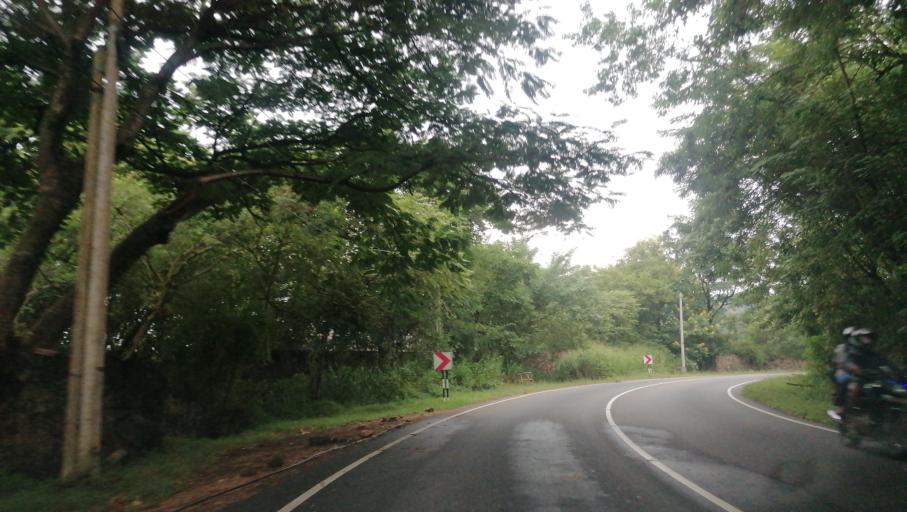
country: LK
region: Central
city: Kandy
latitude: 7.2428
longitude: 80.7284
